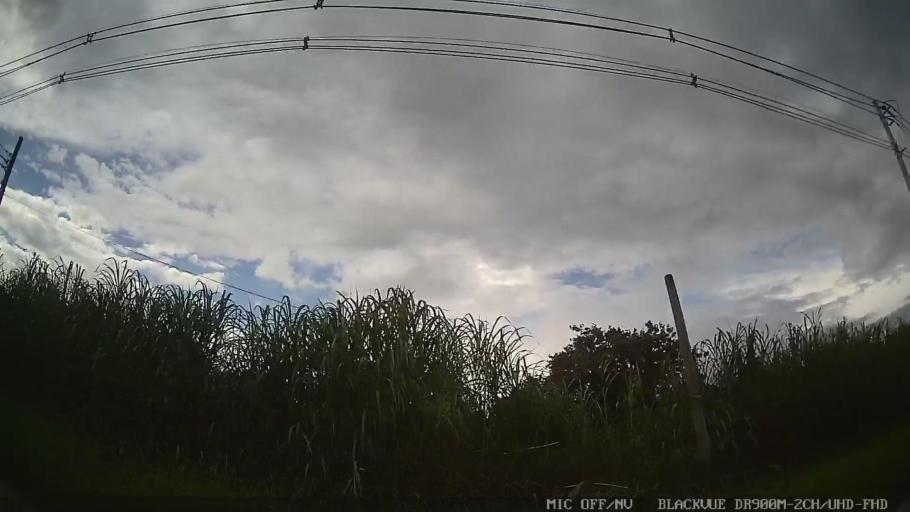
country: BR
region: Sao Paulo
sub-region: Biritiba-Mirim
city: Biritiba Mirim
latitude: -23.5681
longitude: -46.0488
